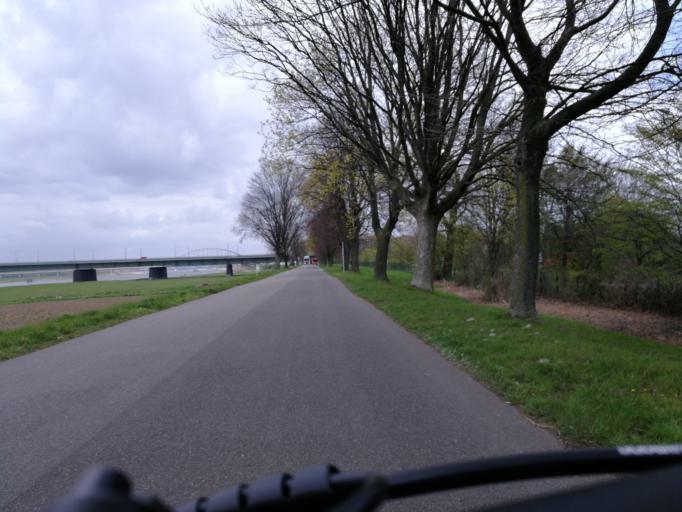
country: DE
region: North Rhine-Westphalia
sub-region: Regierungsbezirk Dusseldorf
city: Dusseldorf
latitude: 51.1948
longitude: 6.7366
